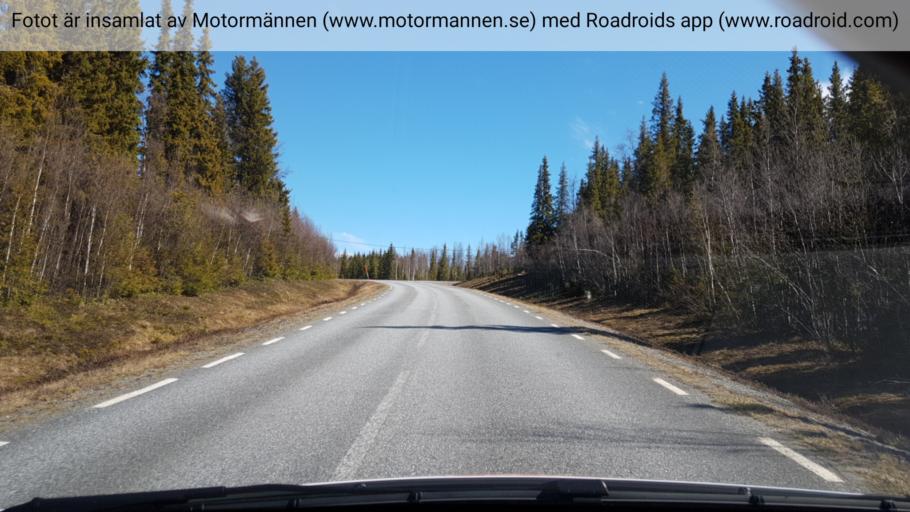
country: SE
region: Vaesterbotten
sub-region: Vilhelmina Kommun
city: Sjoberg
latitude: 65.0342
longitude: 15.8992
